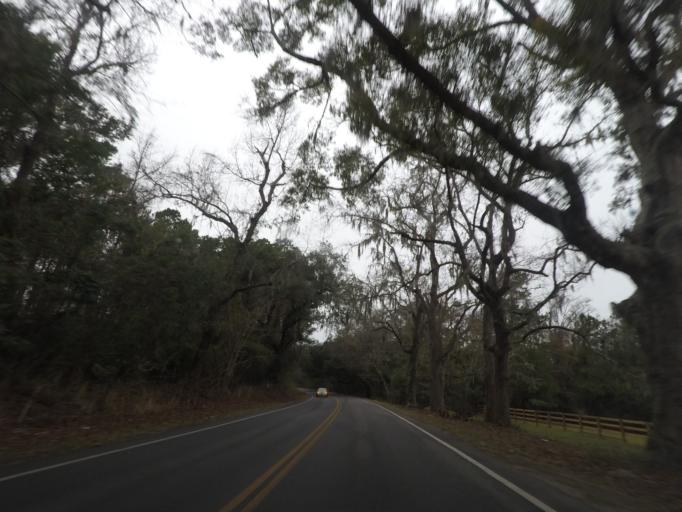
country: US
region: South Carolina
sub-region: Charleston County
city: Seabrook Island
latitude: 32.5808
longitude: -80.3292
